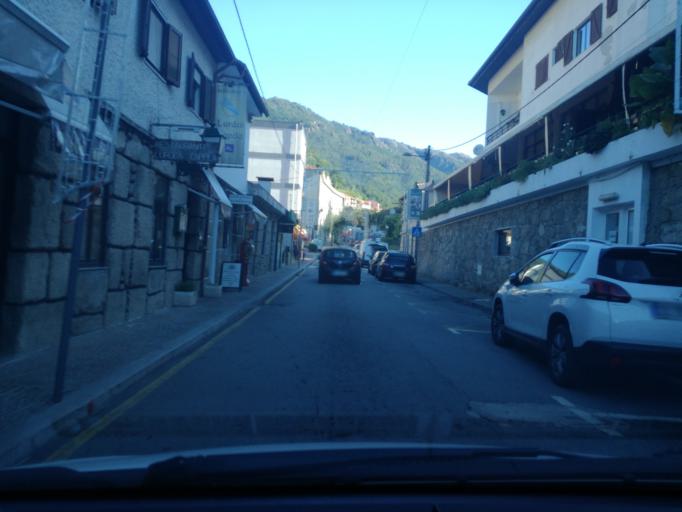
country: PT
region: Braga
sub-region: Vieira do Minho
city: Real
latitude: 41.7257
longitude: -8.1628
